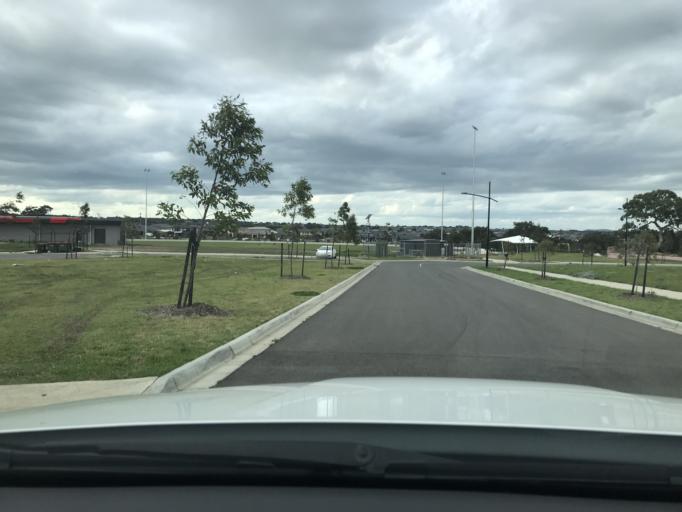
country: AU
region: Victoria
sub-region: Hume
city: Greenvale
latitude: -37.5977
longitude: 144.8913
